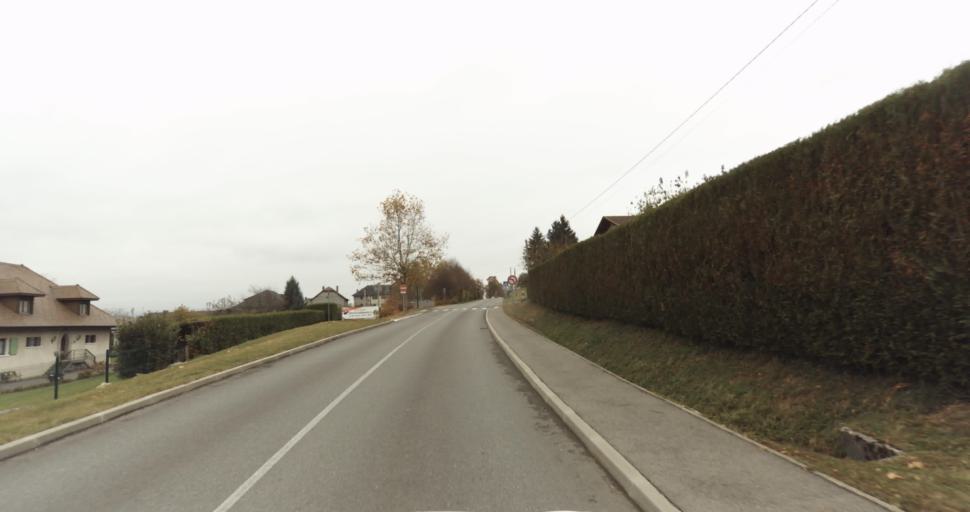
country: FR
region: Rhone-Alpes
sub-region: Departement de la Haute-Savoie
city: Viuz-la-Chiesaz
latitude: 45.8398
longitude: 6.0488
